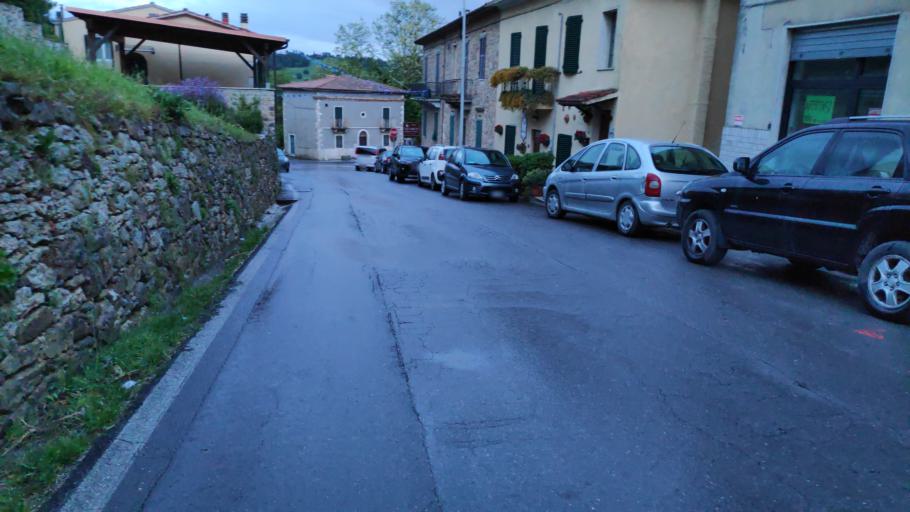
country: IT
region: Tuscany
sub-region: Provincia di Grosseto
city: Manciano
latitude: 42.6204
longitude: 11.4910
